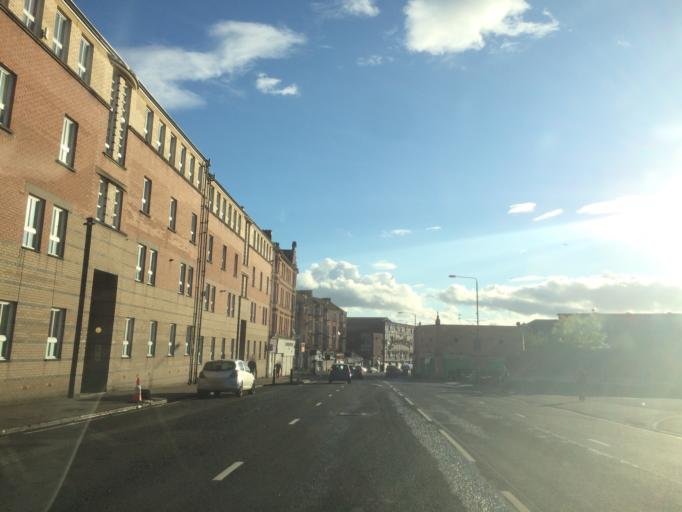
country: GB
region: Scotland
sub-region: Glasgow City
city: Glasgow
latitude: 55.8556
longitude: -4.2336
